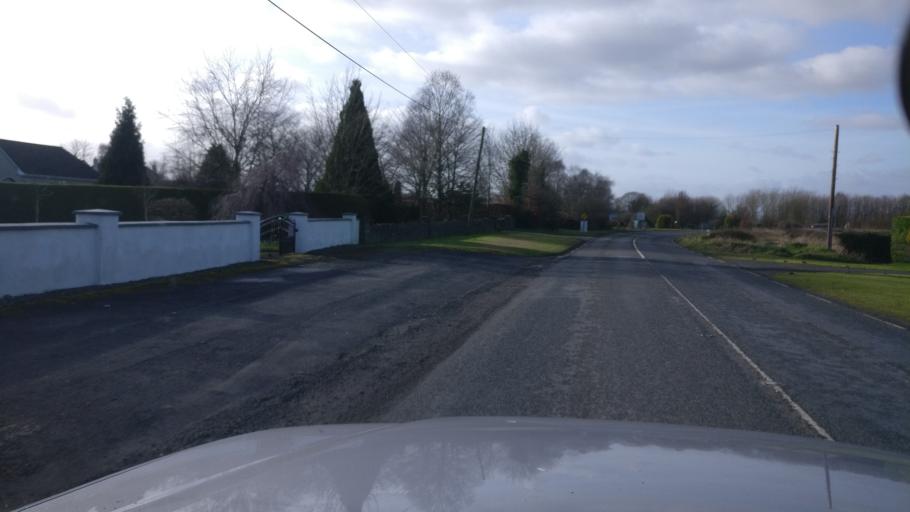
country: IE
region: Leinster
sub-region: Laois
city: Portlaoise
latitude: 53.0109
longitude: -7.2717
